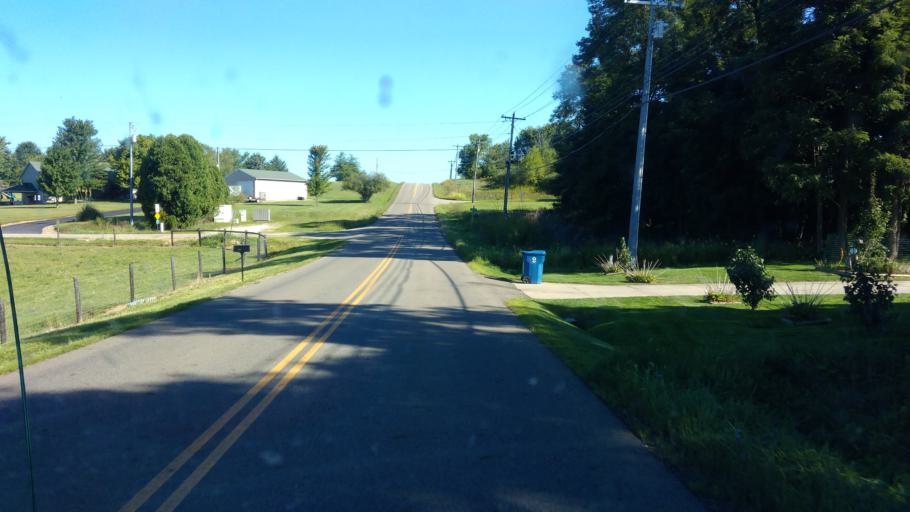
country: US
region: Ohio
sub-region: Knox County
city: Gambier
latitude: 40.4319
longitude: -82.3673
